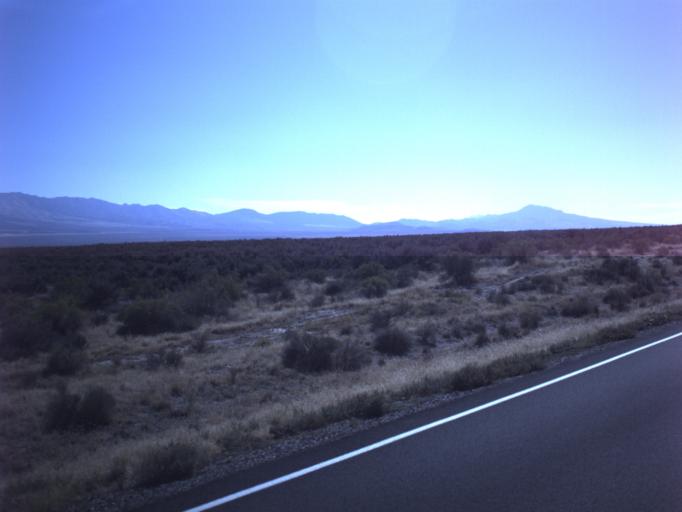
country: US
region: Utah
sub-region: Tooele County
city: Grantsville
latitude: 40.2944
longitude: -112.7425
